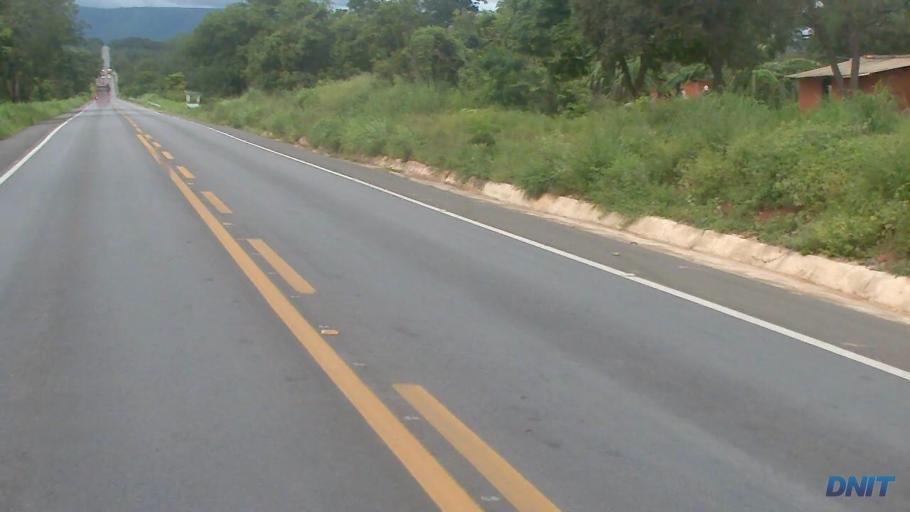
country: BR
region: Goias
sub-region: Posse
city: Posse
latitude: -14.3883
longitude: -46.4477
